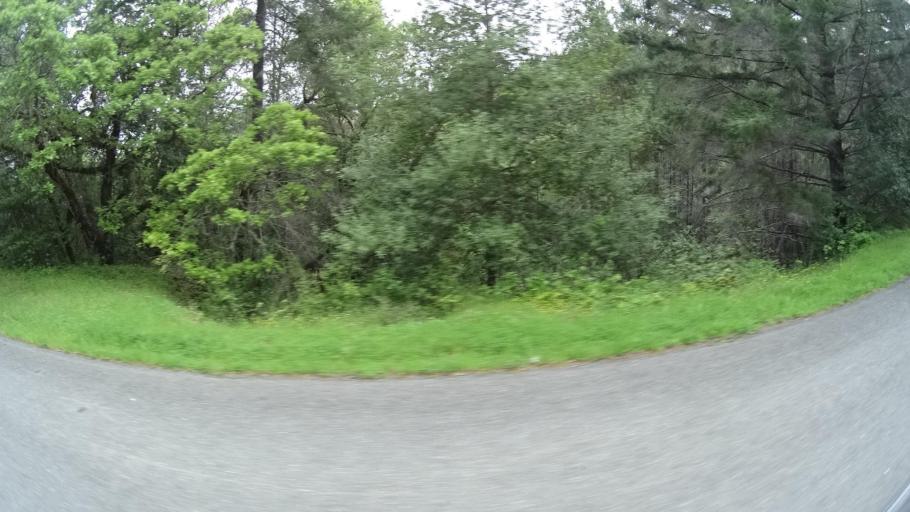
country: US
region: California
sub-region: Humboldt County
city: Redway
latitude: 40.1850
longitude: -123.5822
